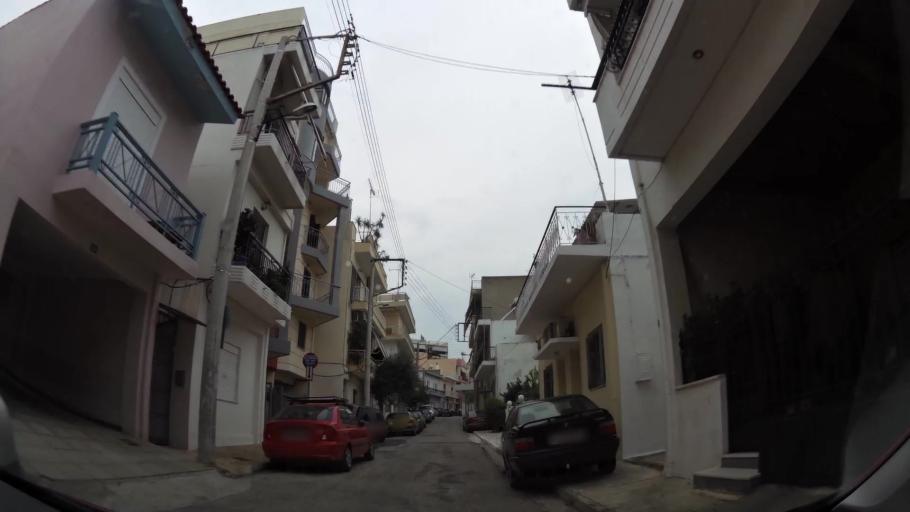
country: GR
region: Attica
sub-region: Nomarchia Athinas
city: Agioi Anargyroi
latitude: 38.0246
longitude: 23.7120
